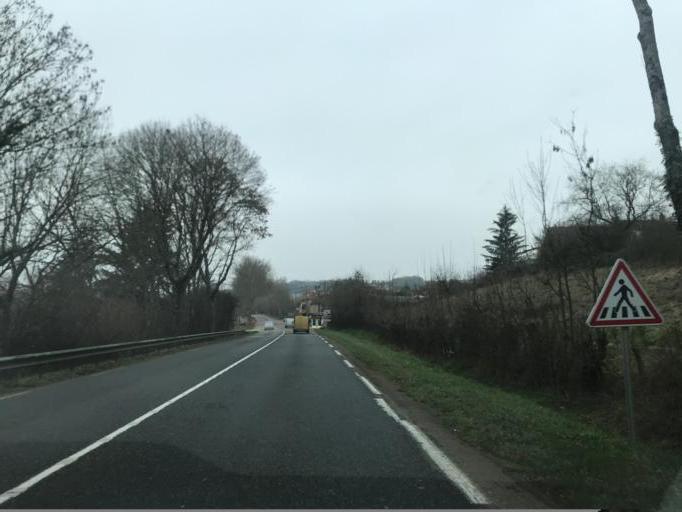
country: FR
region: Bourgogne
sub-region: Departement de l'Yonne
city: Avallon
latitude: 47.5109
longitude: 3.8429
